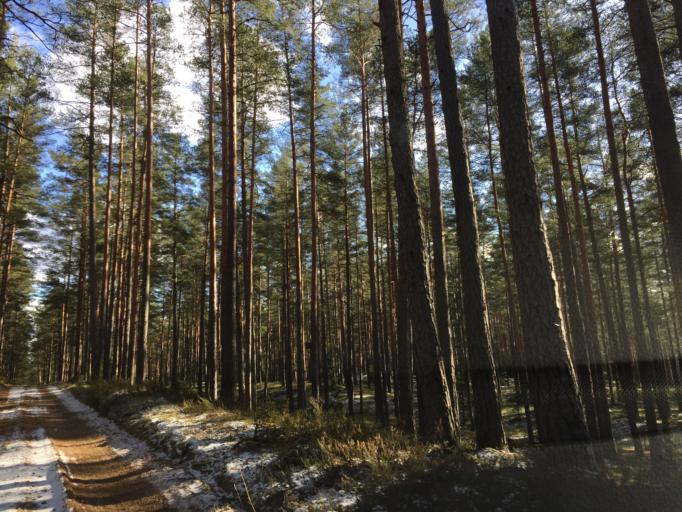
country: LV
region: Garkalne
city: Garkalne
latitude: 56.9639
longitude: 24.4515
